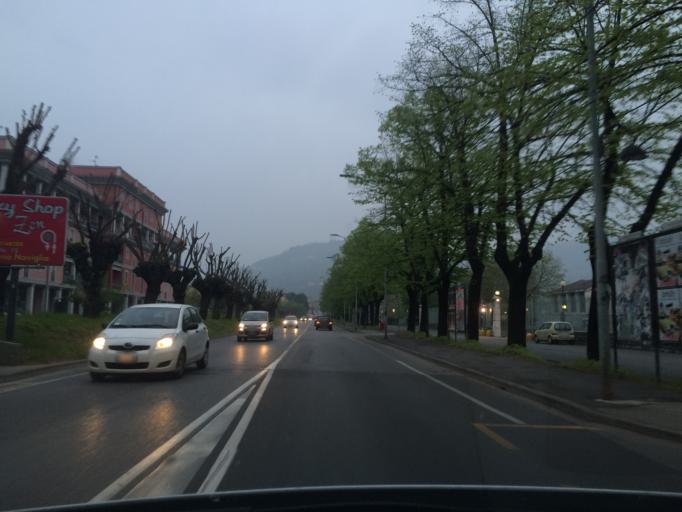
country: IT
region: Lombardy
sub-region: Provincia di Brescia
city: Brescia
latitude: 45.5255
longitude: 10.2317
